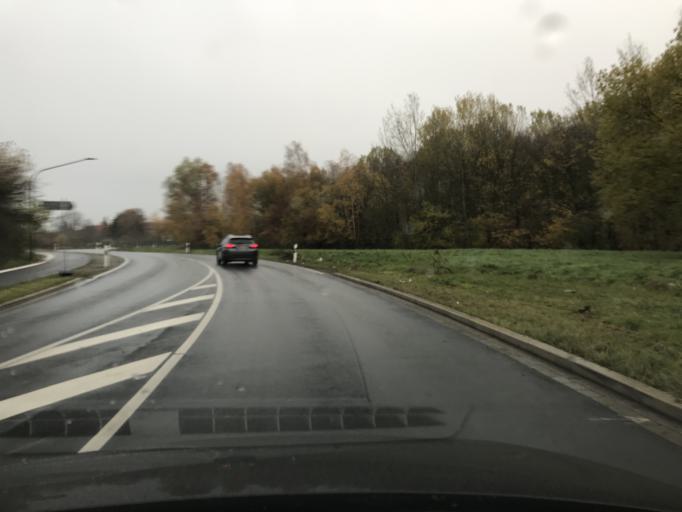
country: DE
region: North Rhine-Westphalia
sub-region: Regierungsbezirk Arnsberg
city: Hamm
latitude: 51.7032
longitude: 7.8138
